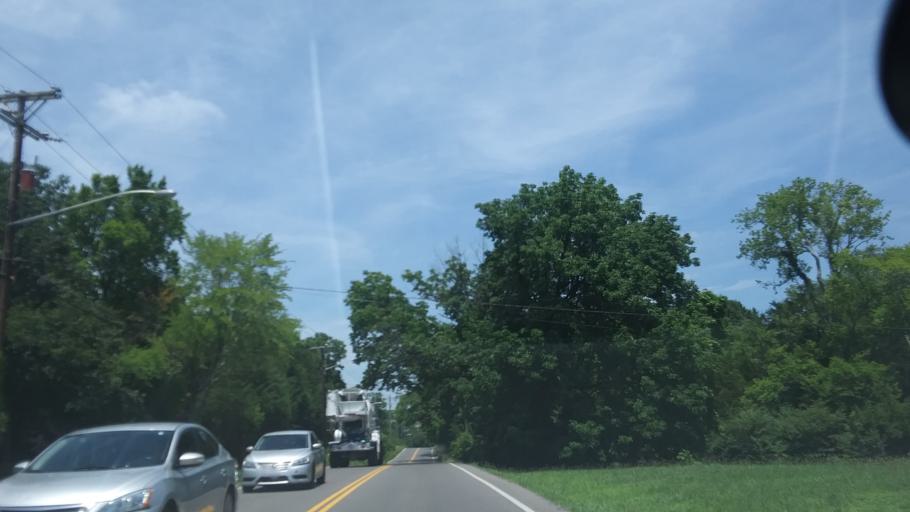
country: US
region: Tennessee
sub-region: Rutherford County
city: La Vergne
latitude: 36.0849
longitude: -86.6282
